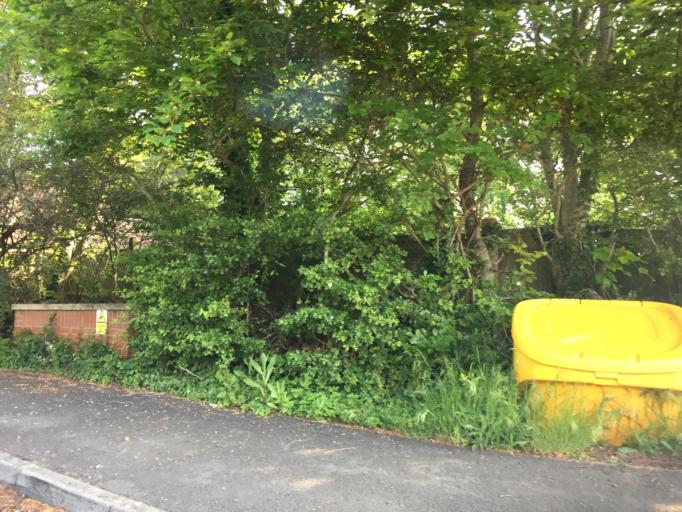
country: GB
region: England
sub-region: Bristol
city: Bristol
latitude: 51.5075
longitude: -2.6076
